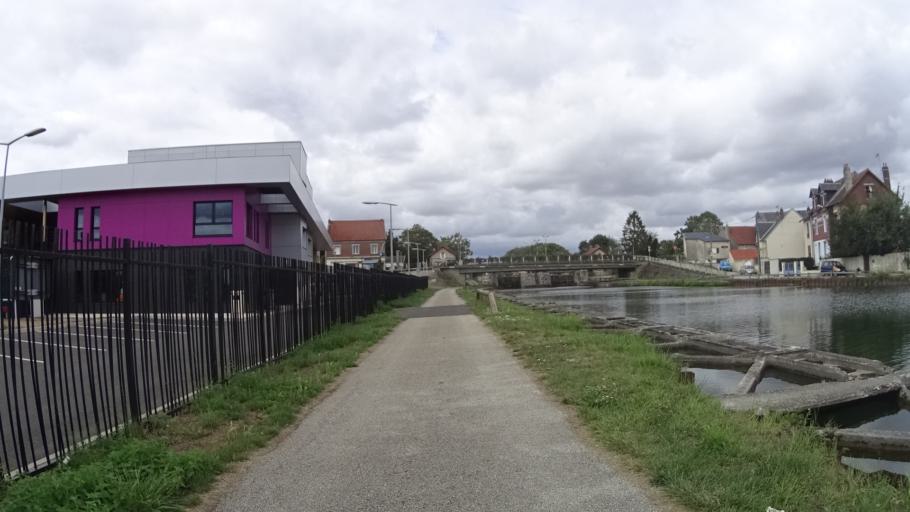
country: FR
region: Picardie
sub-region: Departement de l'Aisne
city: Tergnier
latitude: 49.6555
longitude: 3.3026
